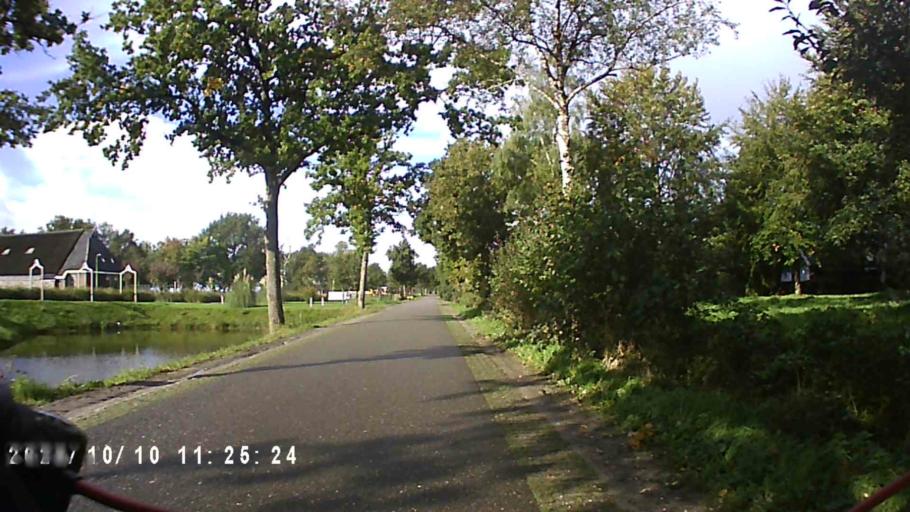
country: NL
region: Friesland
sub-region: Gemeente Smallingerland
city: Drachtstercompagnie
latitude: 53.0876
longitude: 6.1694
